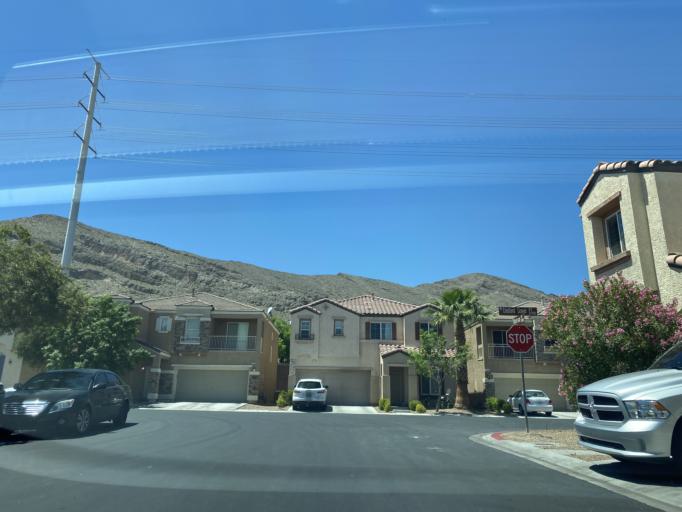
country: US
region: Nevada
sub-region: Clark County
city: Summerlin South
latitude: 36.2286
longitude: -115.3291
